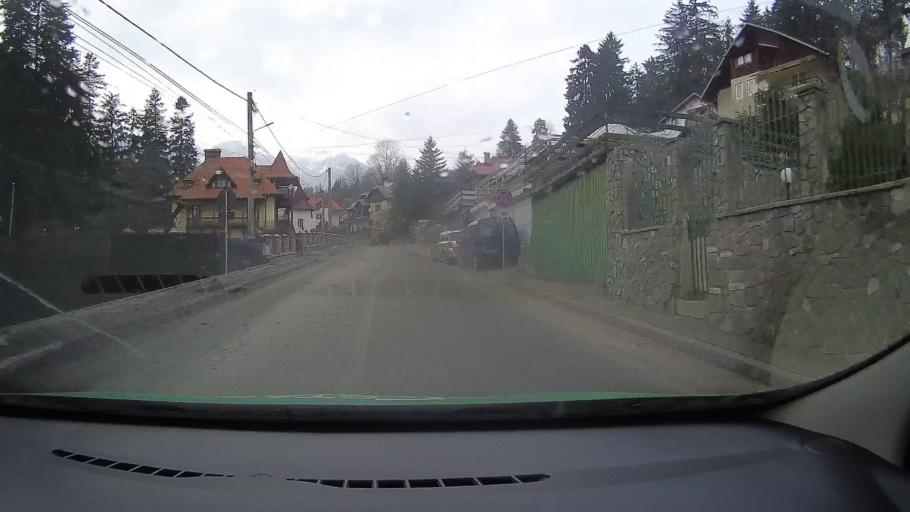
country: RO
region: Prahova
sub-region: Oras Sinaia
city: Sinaia
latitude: 45.3534
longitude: 25.5455
